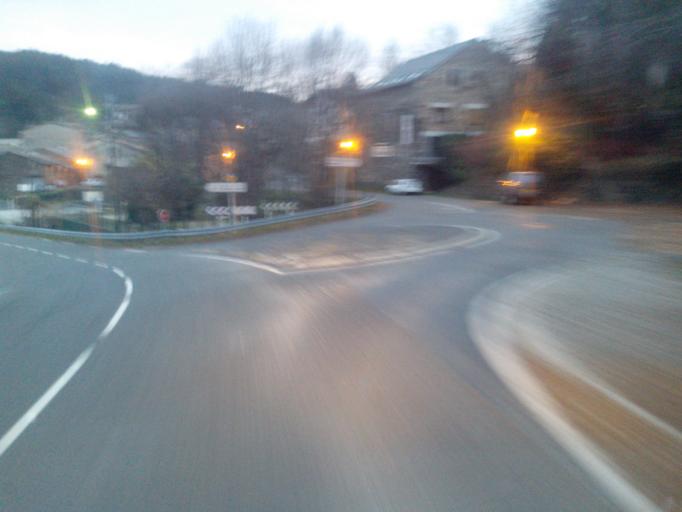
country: FR
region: Languedoc-Roussillon
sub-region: Departement du Gard
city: Saint-Jean-du-Gard
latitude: 44.1486
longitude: 3.7709
